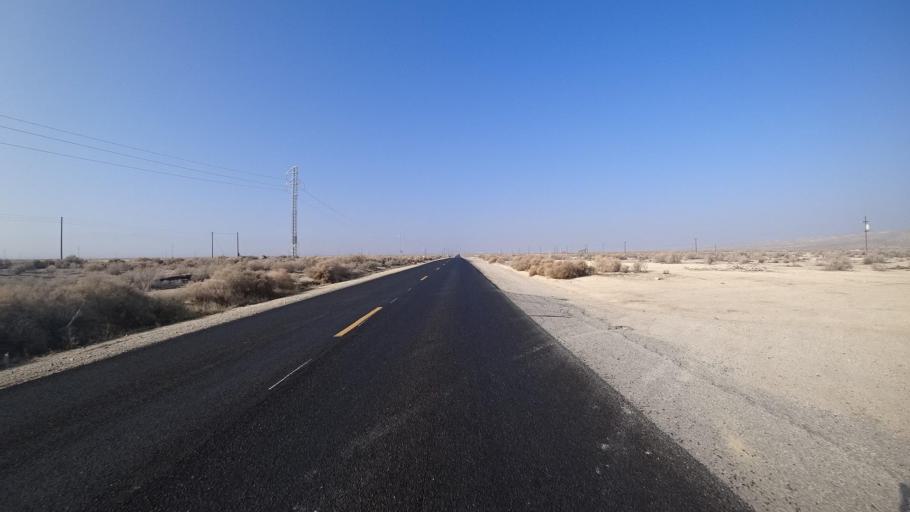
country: US
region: California
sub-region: Kern County
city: Ford City
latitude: 35.1806
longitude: -119.4777
